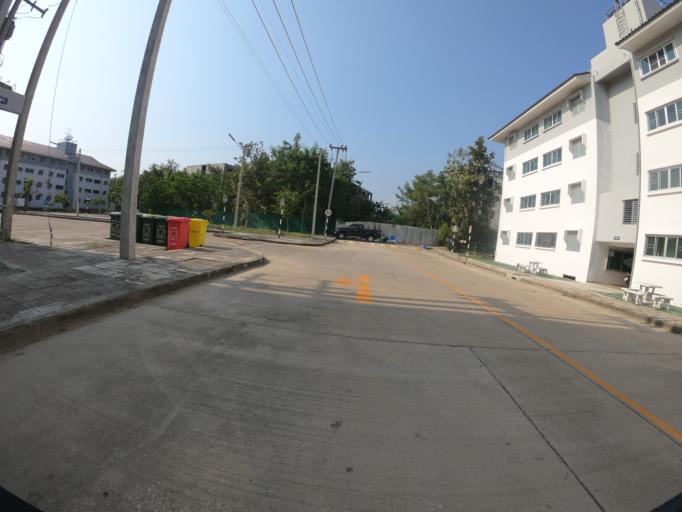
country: TH
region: Chiang Mai
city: Hang Dong
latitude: 18.7358
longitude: 98.9393
